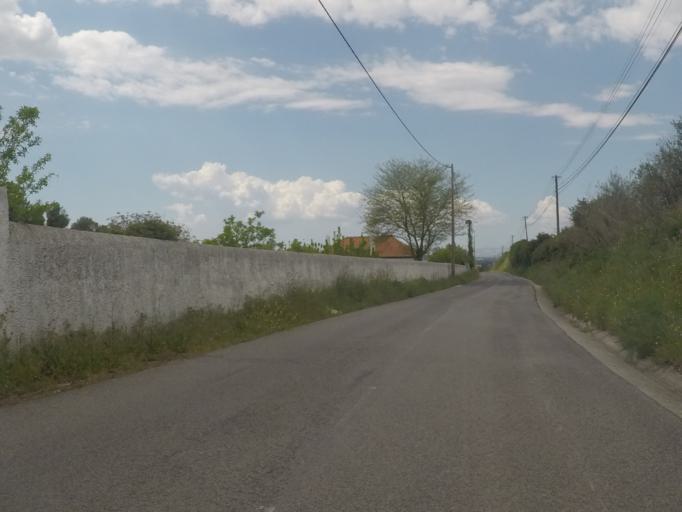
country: PT
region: Setubal
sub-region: Palmela
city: Quinta do Anjo
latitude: 38.5123
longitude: -9.0063
